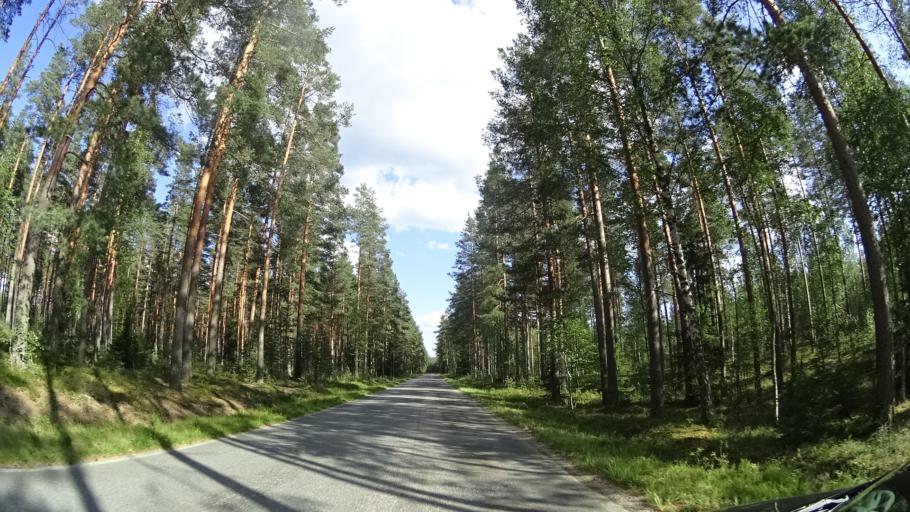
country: FI
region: Uusimaa
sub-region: Helsinki
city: Kaerkoelae
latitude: 60.7426
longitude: 24.0840
